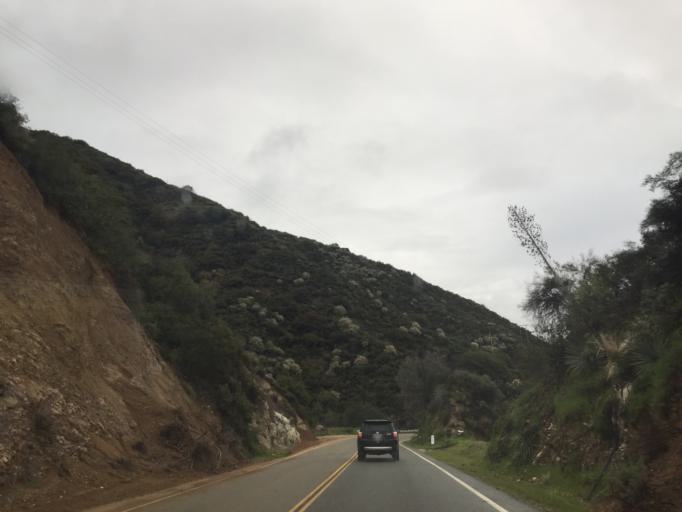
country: US
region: California
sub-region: Los Angeles County
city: Glendora
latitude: 34.2232
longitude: -117.8513
